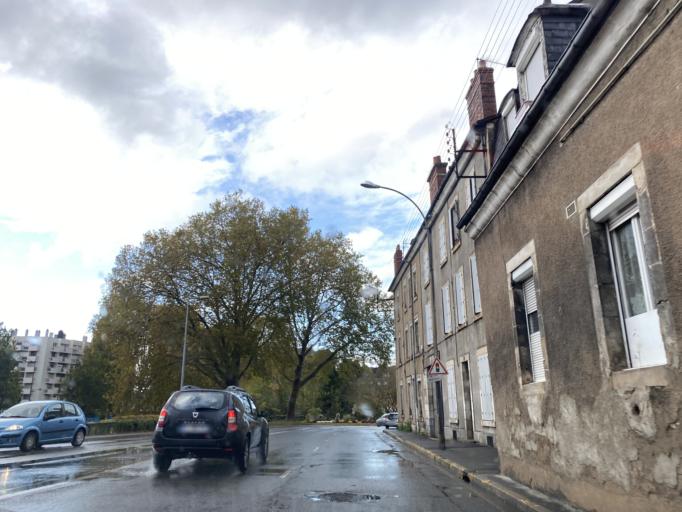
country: FR
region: Centre
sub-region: Departement du Cher
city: Bourges
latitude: 47.0799
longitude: 2.3900
